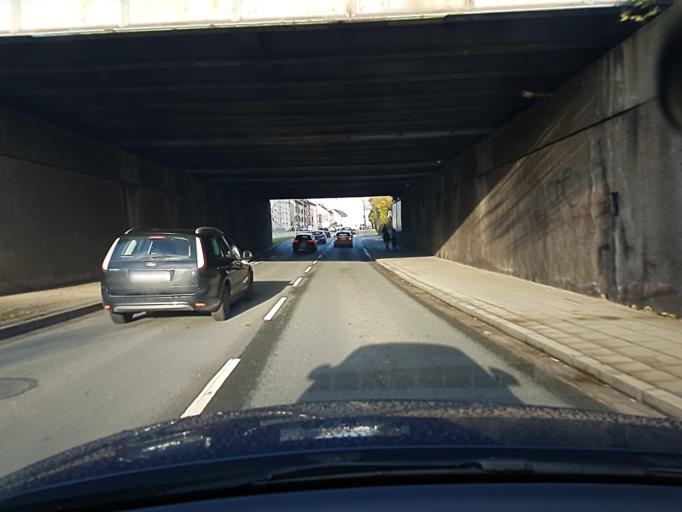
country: DE
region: North Rhine-Westphalia
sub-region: Regierungsbezirk Dusseldorf
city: Essen
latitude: 51.4827
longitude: 7.0010
